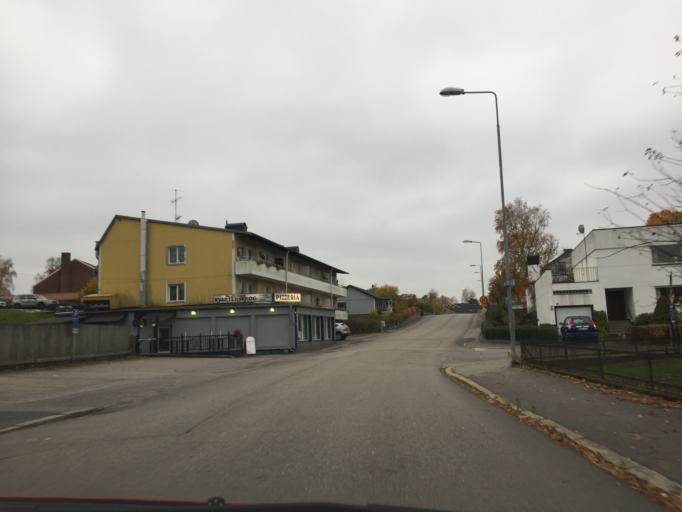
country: SE
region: Vaestra Goetaland
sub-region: Trollhattan
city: Trollhattan
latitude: 58.2625
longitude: 12.2735
